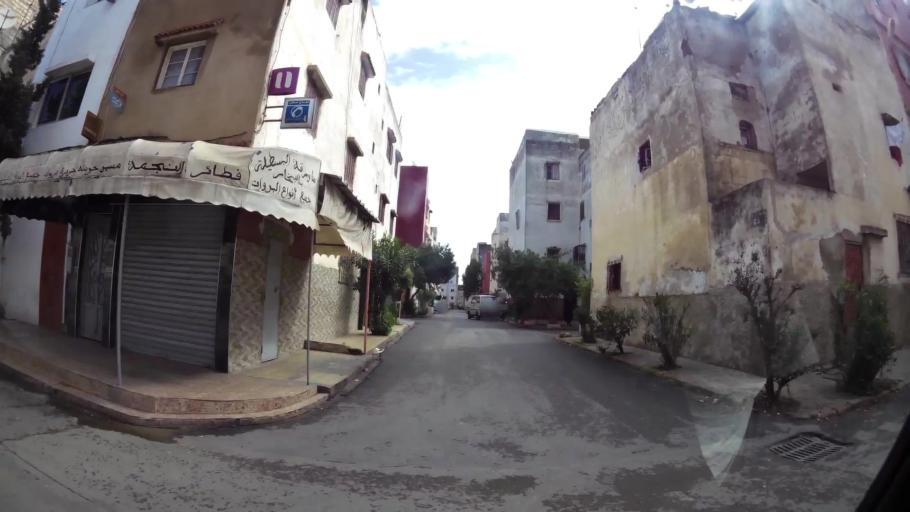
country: MA
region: Grand Casablanca
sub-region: Casablanca
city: Casablanca
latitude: 33.5740
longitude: -7.6761
